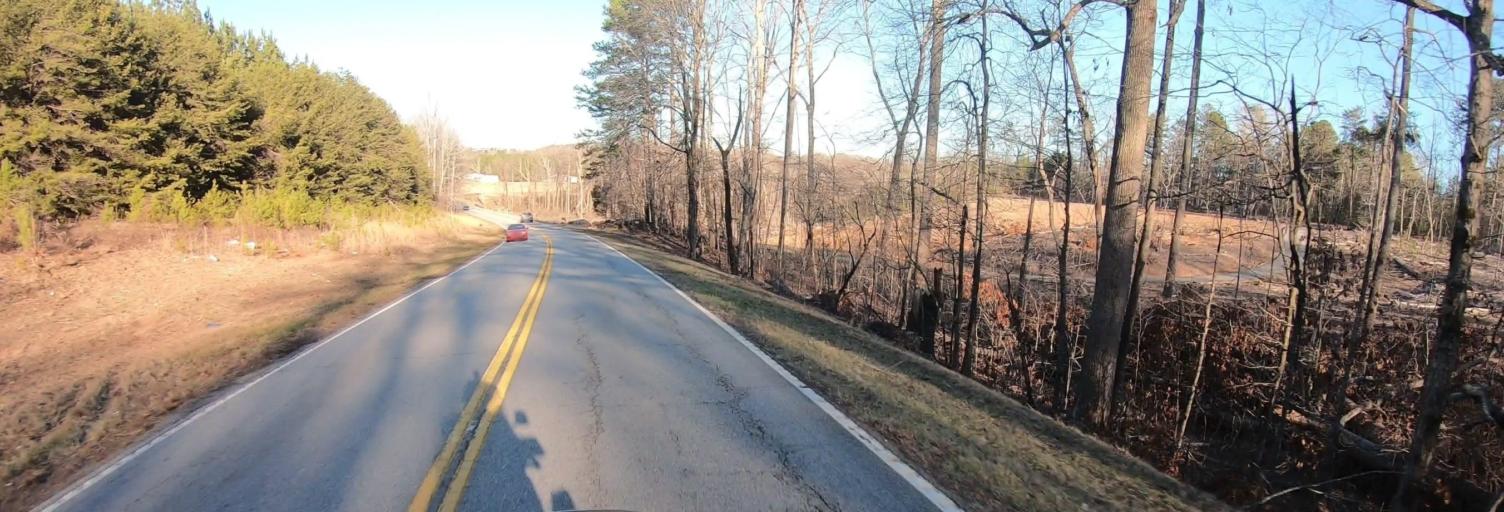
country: US
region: South Carolina
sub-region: Spartanburg County
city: Landrum
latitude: 35.1298
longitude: -82.1254
